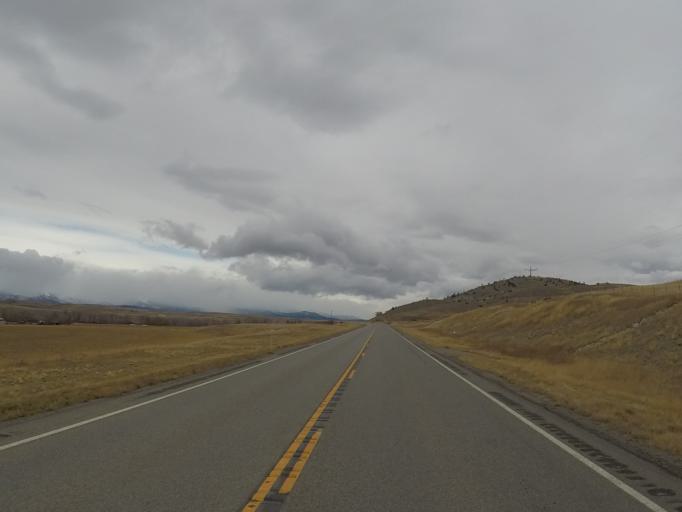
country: US
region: Montana
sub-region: Sweet Grass County
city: Big Timber
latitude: 45.8728
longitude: -109.9476
